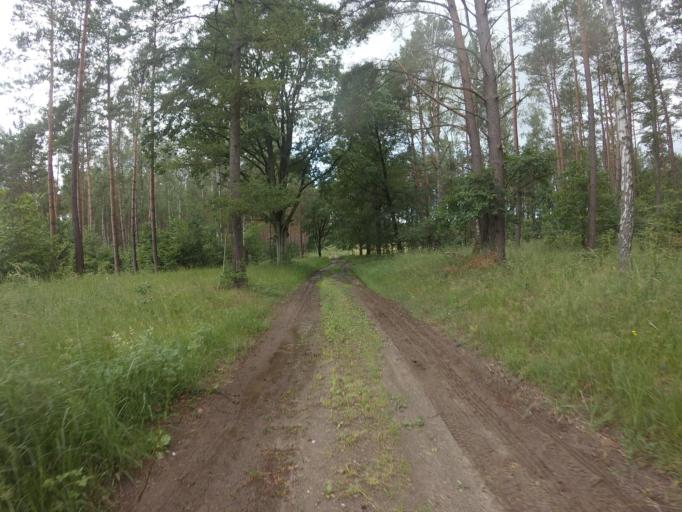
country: PL
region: West Pomeranian Voivodeship
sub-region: Powiat choszczenski
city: Krzecin
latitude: 53.0392
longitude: 15.5694
